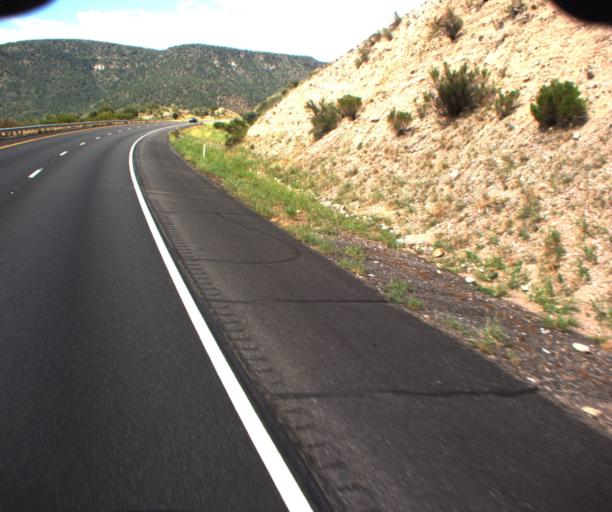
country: US
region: Arizona
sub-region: Yavapai County
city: Camp Verde
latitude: 34.5420
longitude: -111.9091
